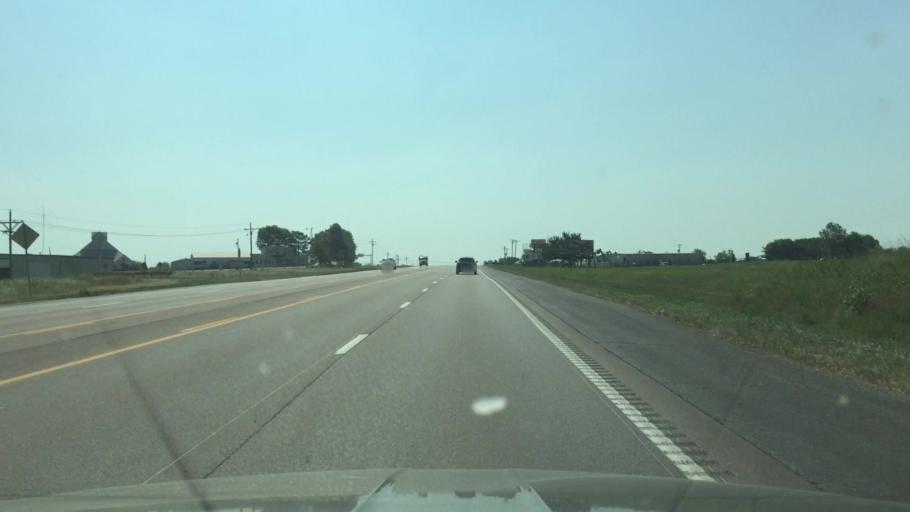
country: US
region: Missouri
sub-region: Pettis County
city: Sedalia
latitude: 38.7189
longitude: -93.2943
